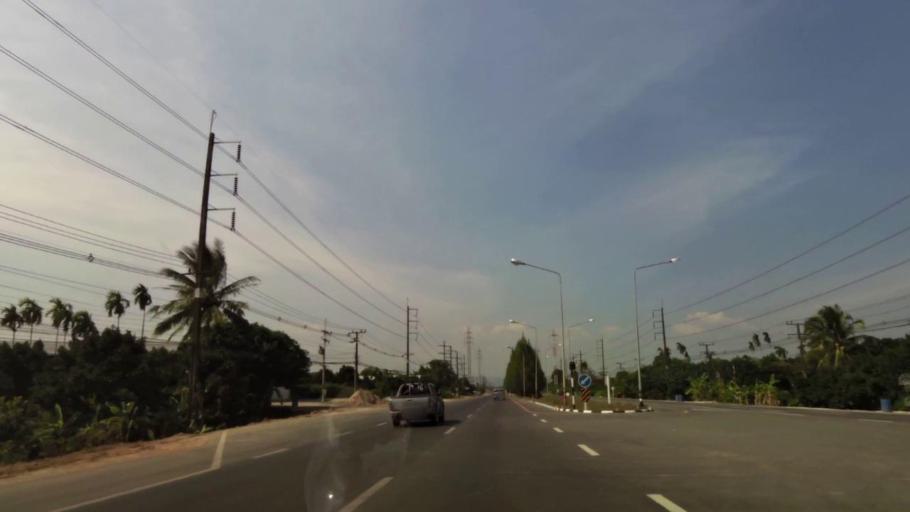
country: TH
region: Chanthaburi
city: Chanthaburi
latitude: 12.6341
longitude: 102.1405
